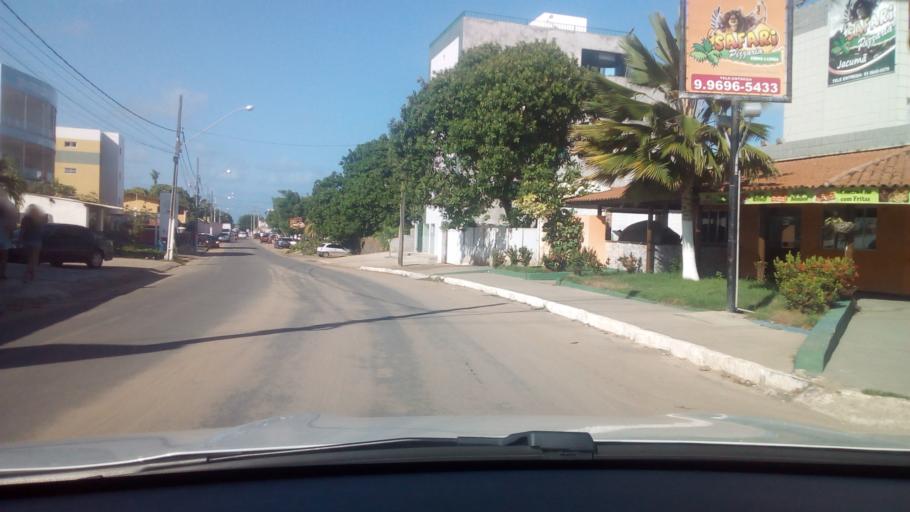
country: BR
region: Paraiba
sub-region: Conde
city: Conde
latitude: -7.2889
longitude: -34.8032
